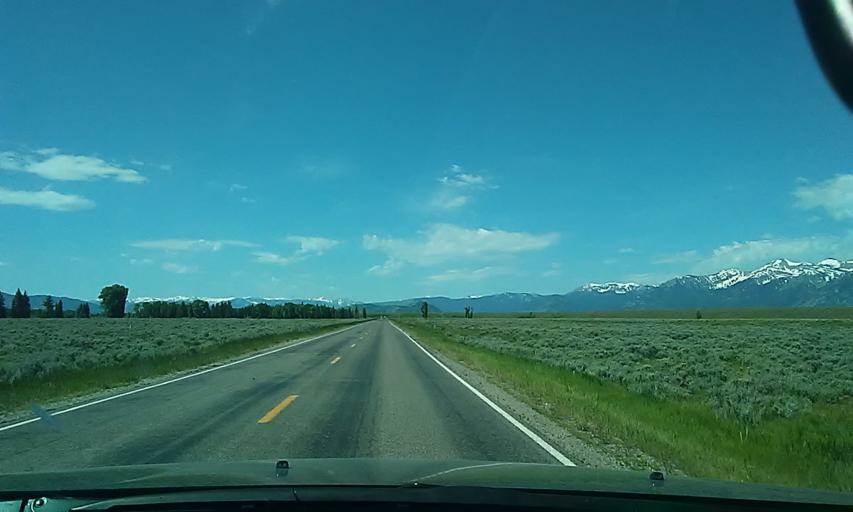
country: US
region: Wyoming
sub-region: Teton County
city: Jackson
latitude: 43.6131
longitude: -110.6807
